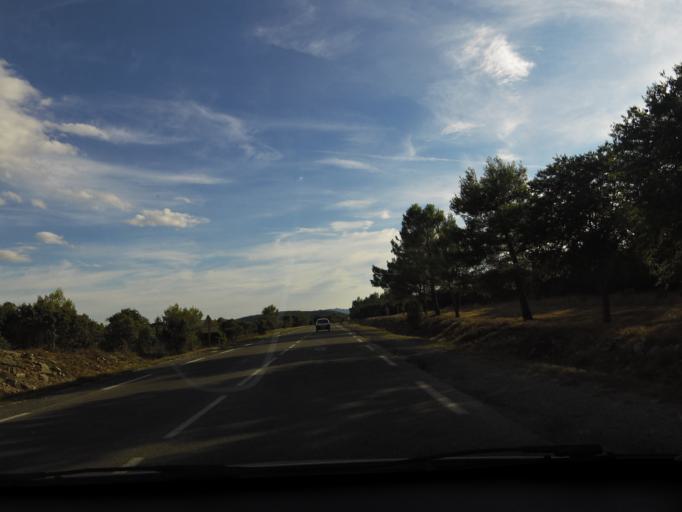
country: FR
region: Languedoc-Roussillon
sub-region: Departement du Gard
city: Quissac
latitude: 43.8770
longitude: 3.9619
